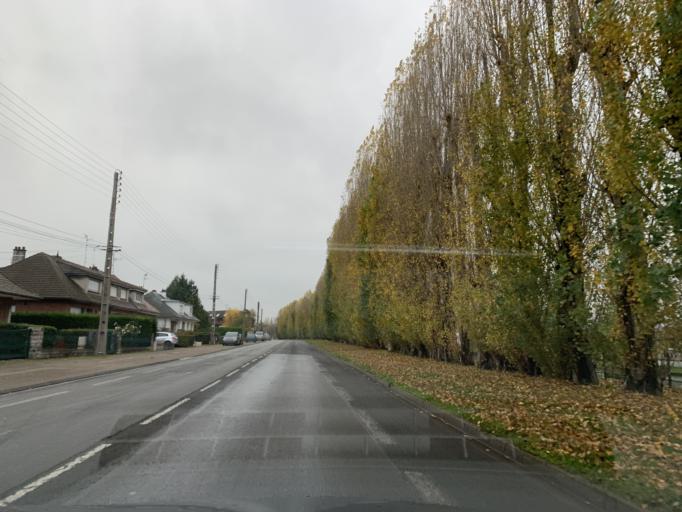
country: FR
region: Nord-Pas-de-Calais
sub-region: Departement du Nord
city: Neuville-Saint-Remy
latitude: 50.1793
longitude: 3.2244
